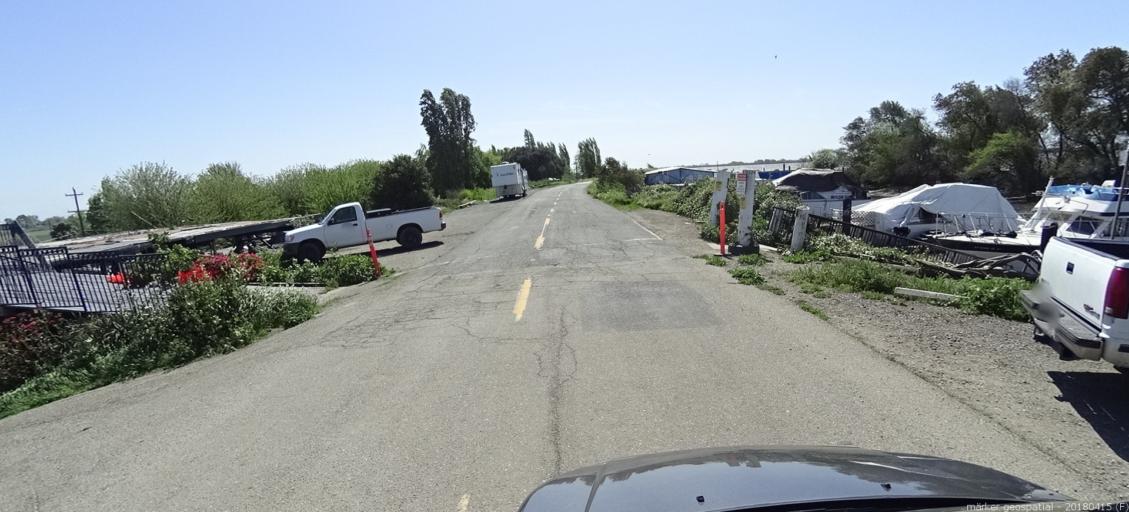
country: US
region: California
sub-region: Contra Costa County
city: Bethel Island
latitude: 38.1050
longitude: -121.5936
